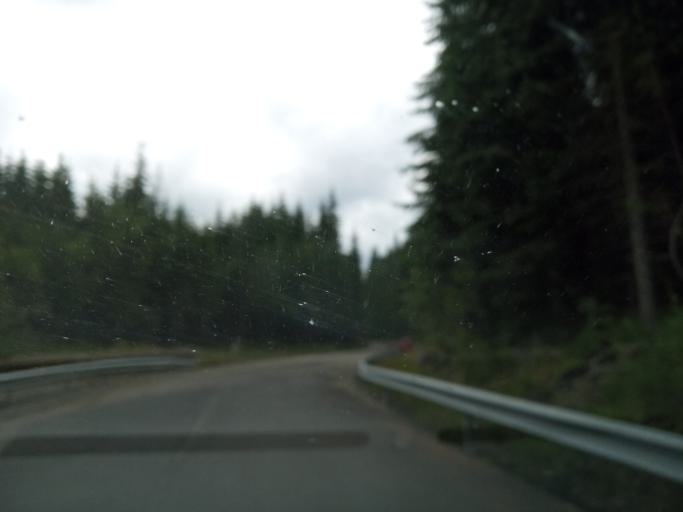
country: RO
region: Valcea
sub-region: Comuna Voineasa
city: Voineasa
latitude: 45.4135
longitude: 23.7261
